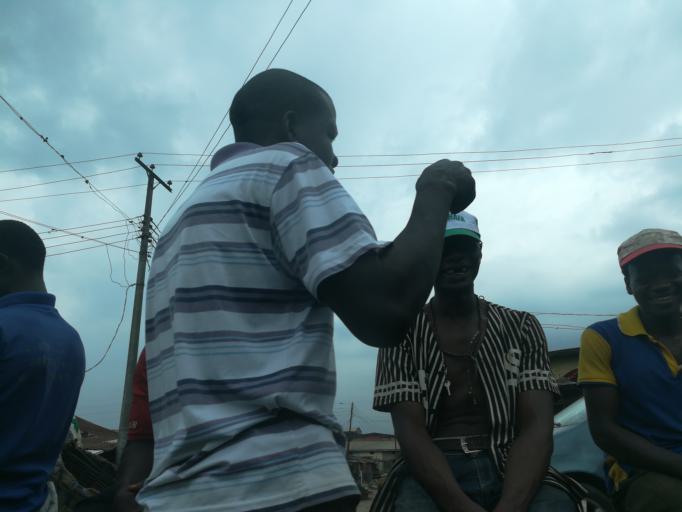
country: NG
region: Lagos
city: Ojota
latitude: 6.6099
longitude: 3.3962
